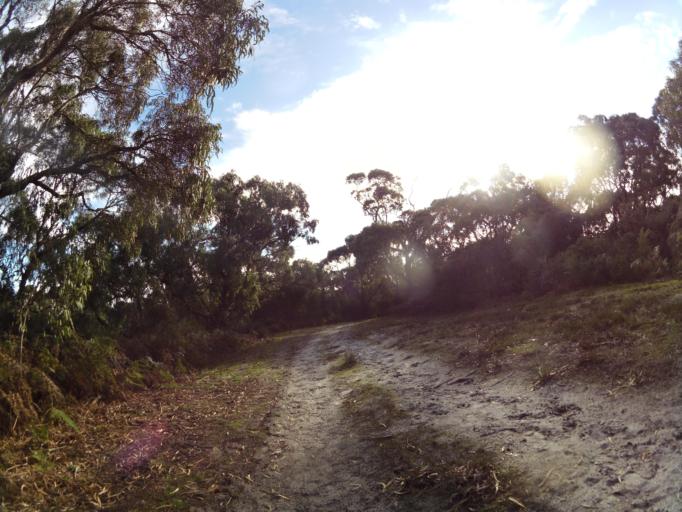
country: AU
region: Victoria
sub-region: Bass Coast
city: North Wonthaggi
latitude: -38.6316
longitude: 145.5701
